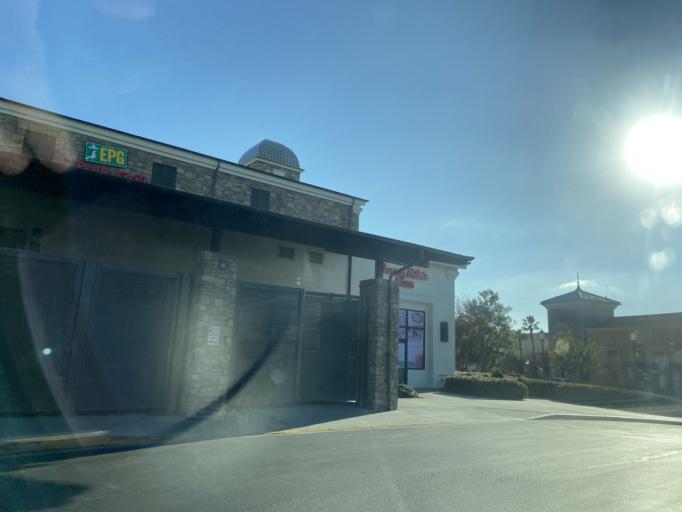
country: US
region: California
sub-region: San Diego County
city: Bonita
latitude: 32.6248
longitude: -116.9650
